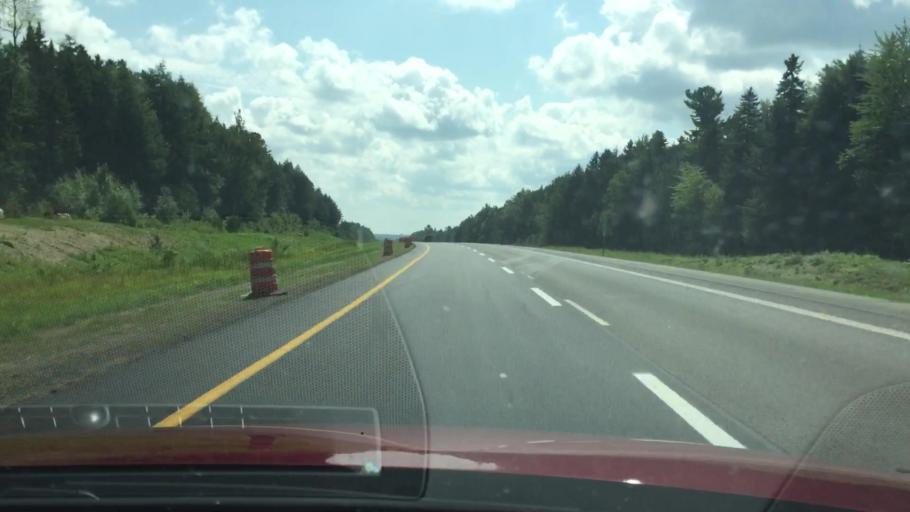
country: US
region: Maine
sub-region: Penobscot County
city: Medway
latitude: 45.6707
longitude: -68.4994
